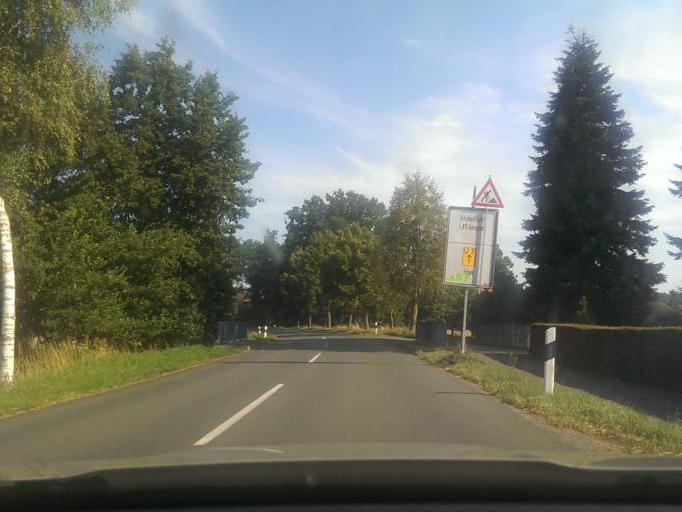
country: DE
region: North Rhine-Westphalia
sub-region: Regierungsbezirk Detmold
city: Delbruck
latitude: 51.7473
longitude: 8.5830
